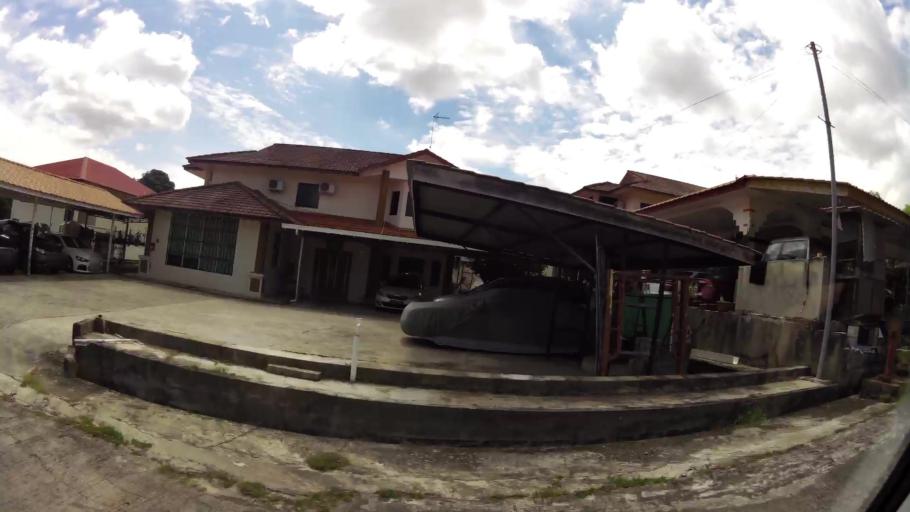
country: BN
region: Brunei and Muara
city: Bandar Seri Begawan
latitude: 4.9354
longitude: 114.8934
